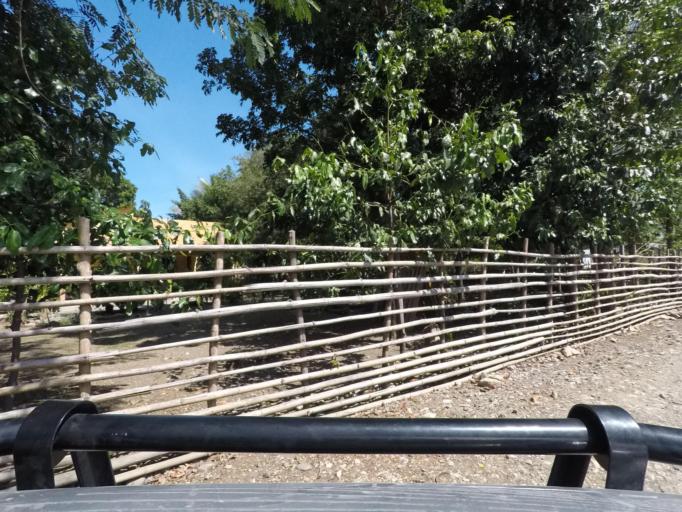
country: TL
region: Liquica
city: Maubara
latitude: -8.7882
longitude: 125.1030
